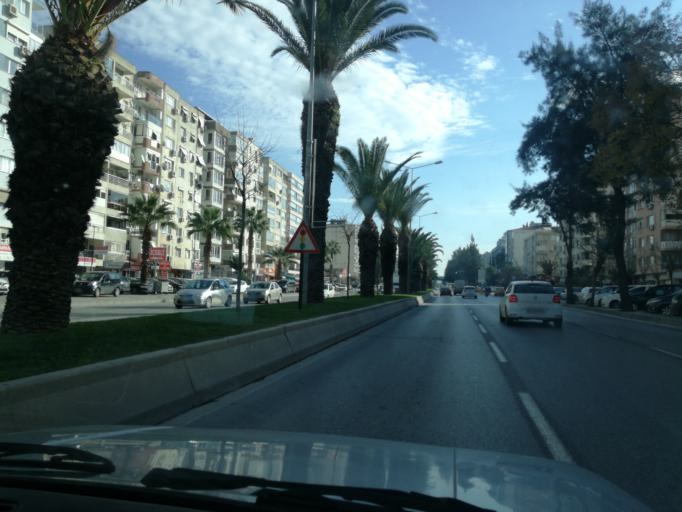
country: TR
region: Izmir
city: Izmir
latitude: 38.4019
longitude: 27.1250
